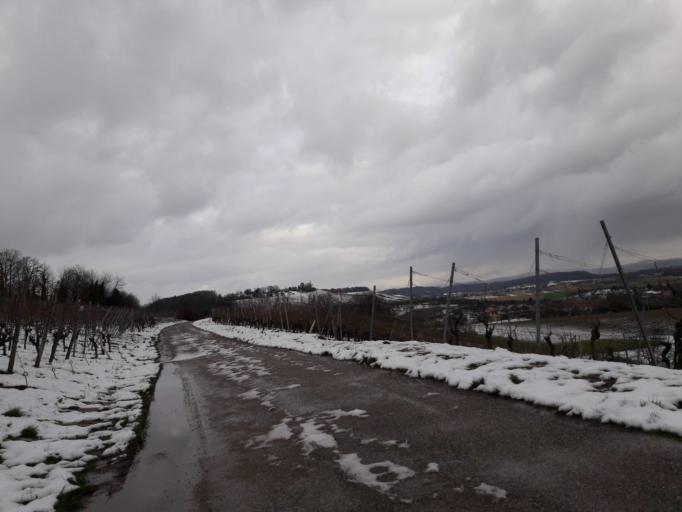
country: DE
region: Baden-Wuerttemberg
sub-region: Regierungsbezirk Stuttgart
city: Oberstenfeld
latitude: 48.9964
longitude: 9.3496
